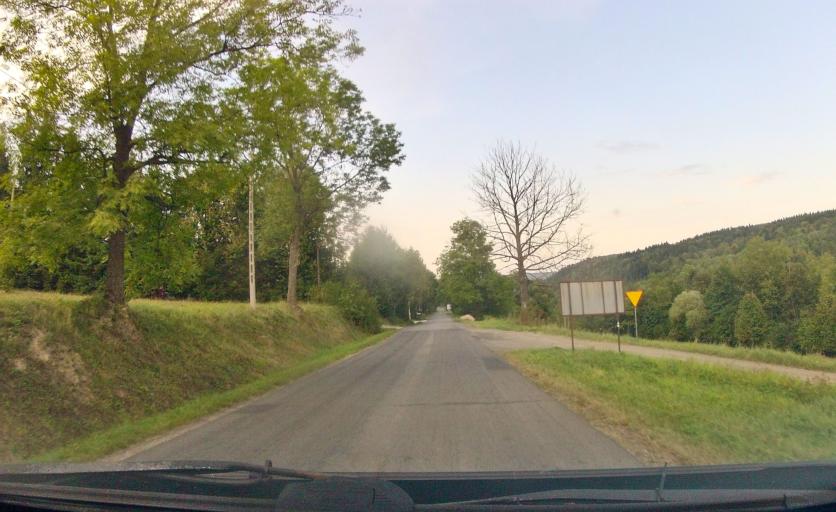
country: PL
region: Subcarpathian Voivodeship
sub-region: Powiat krosnienski
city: Dukla
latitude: 49.5339
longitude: 21.6151
